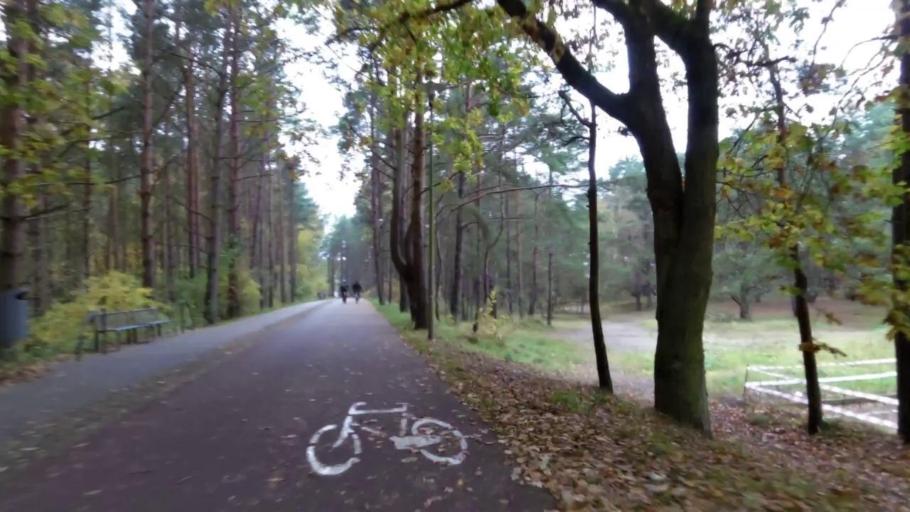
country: PL
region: West Pomeranian Voivodeship
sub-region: Swinoujscie
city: Swinoujscie
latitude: 53.9258
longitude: 14.2282
